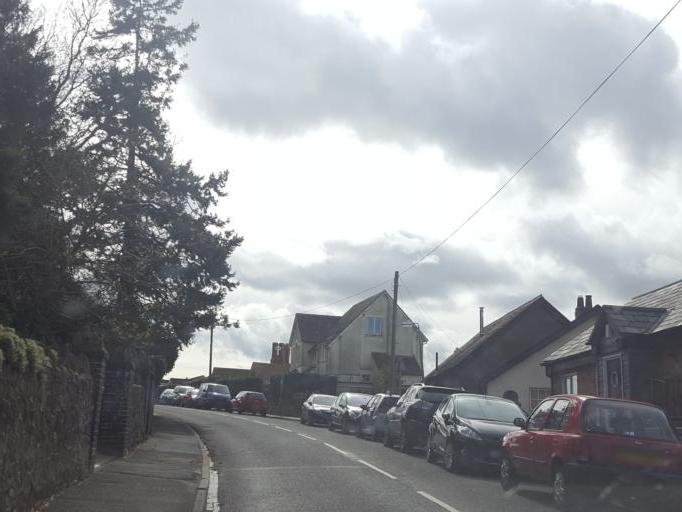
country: GB
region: England
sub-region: Worcestershire
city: Great Malvern
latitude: 52.1162
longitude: -2.3472
